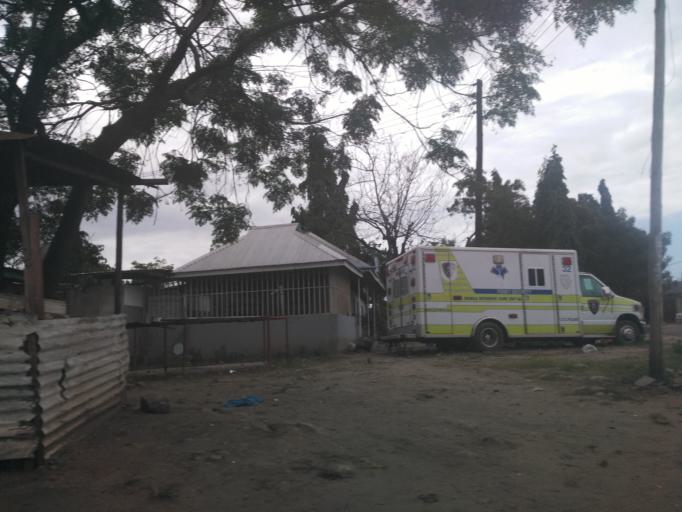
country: TZ
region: Dar es Salaam
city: Magomeni
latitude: -6.7939
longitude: 39.2694
